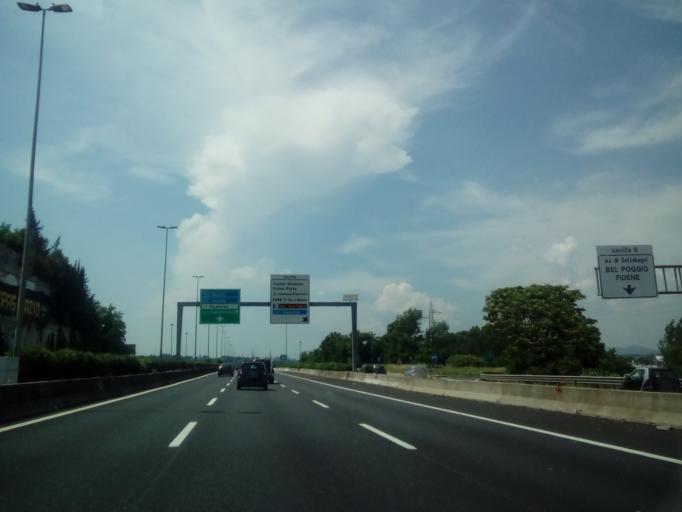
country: IT
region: Latium
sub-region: Citta metropolitana di Roma Capitale
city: Monte Caminetto
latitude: 41.9872
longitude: 12.5172
